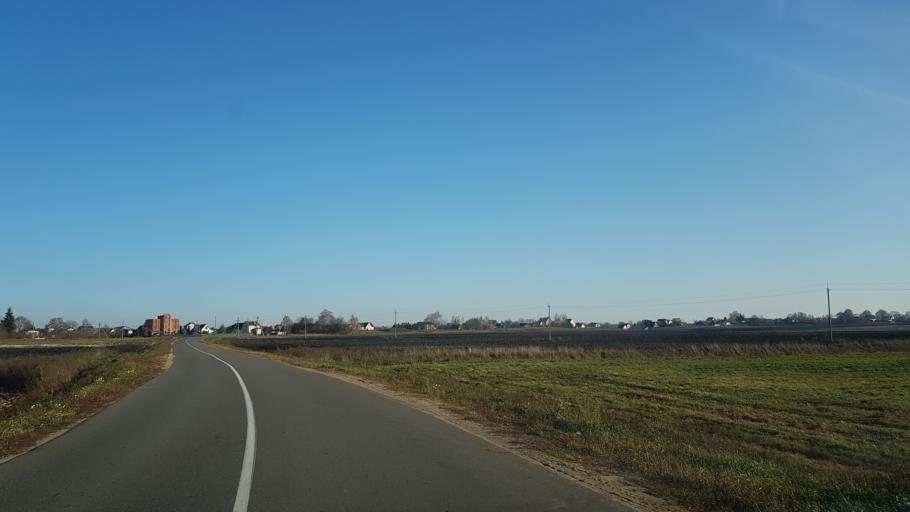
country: BY
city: Fanipol
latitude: 53.7203
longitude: 27.3057
